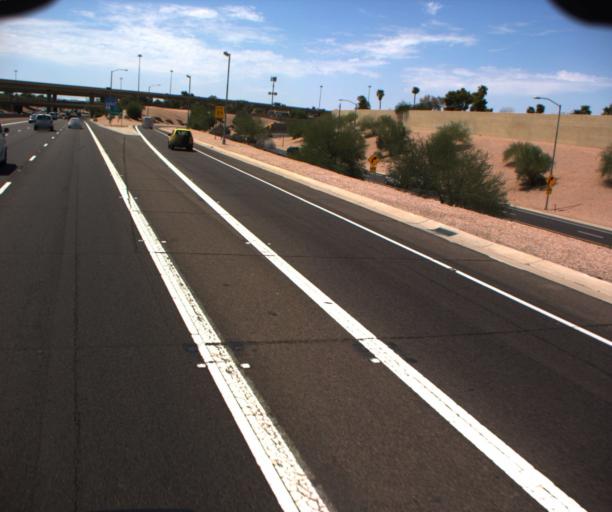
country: US
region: Arizona
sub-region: Maricopa County
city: Tempe
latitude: 33.3859
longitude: -111.8863
